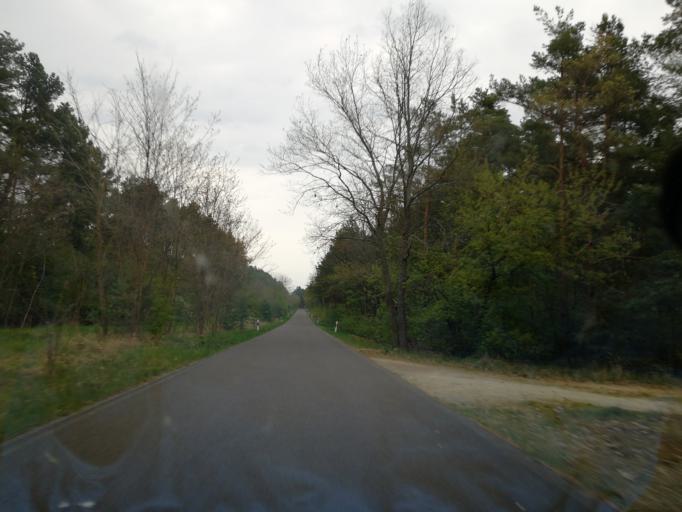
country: DE
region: Brandenburg
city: Lubbenau
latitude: 51.8122
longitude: 13.8918
